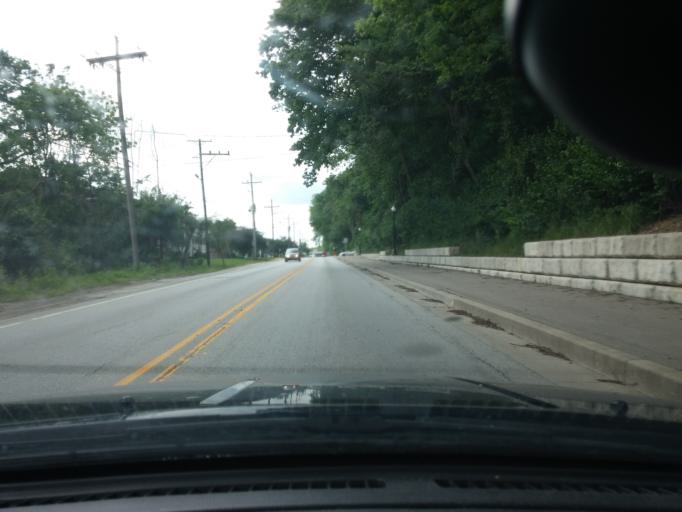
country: US
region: Indiana
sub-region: Tippecanoe County
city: West Lafayette
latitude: 40.4332
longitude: -86.8986
